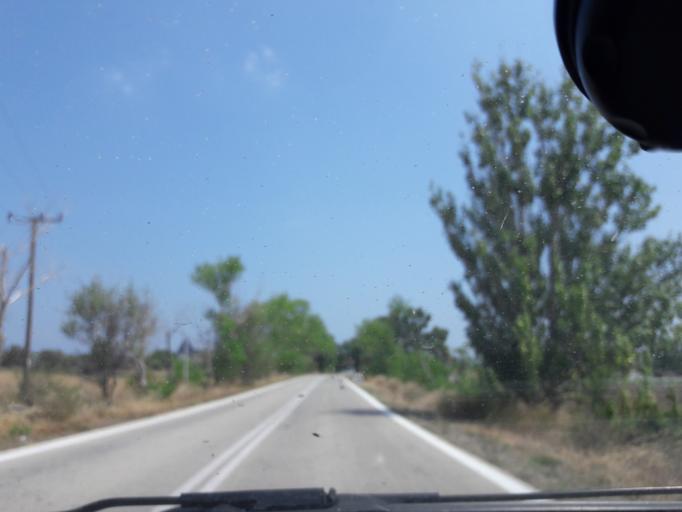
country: GR
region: North Aegean
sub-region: Nomos Lesvou
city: Myrina
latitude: 39.9243
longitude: 25.3280
